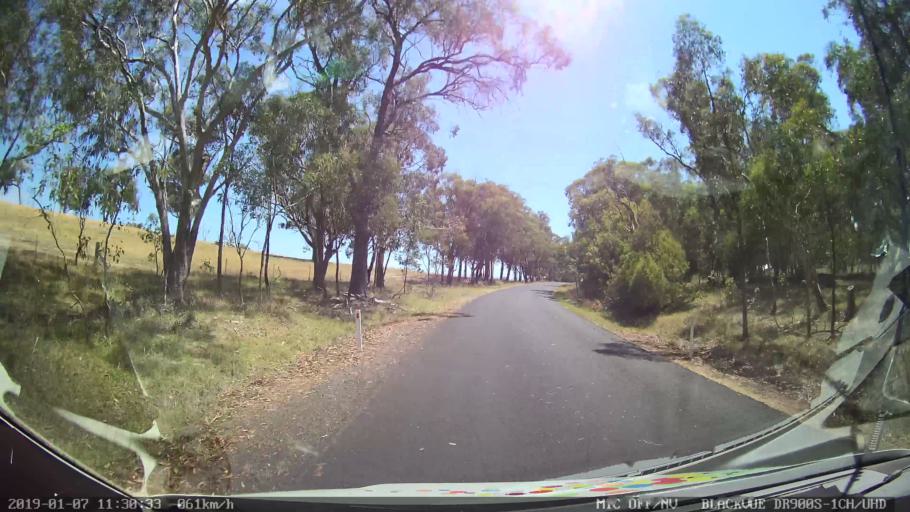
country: AU
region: New South Wales
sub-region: Armidale Dumaresq
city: Armidale
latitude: -30.4281
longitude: 151.5632
